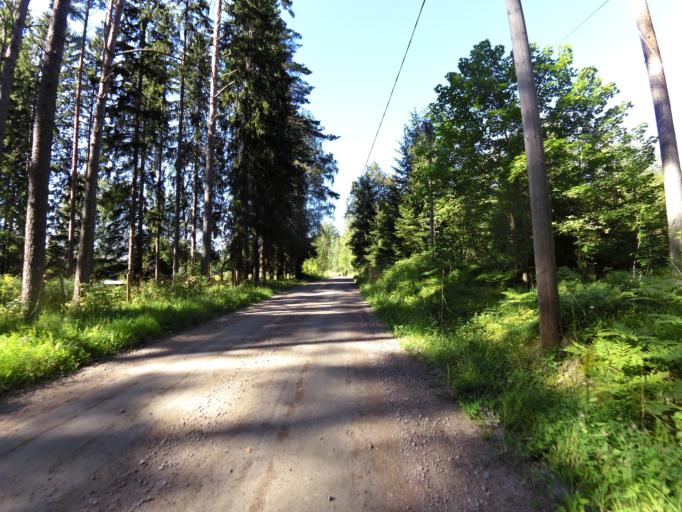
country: SE
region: Gaevleborg
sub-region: Hofors Kommun
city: Hofors
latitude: 60.5318
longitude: 16.4134
